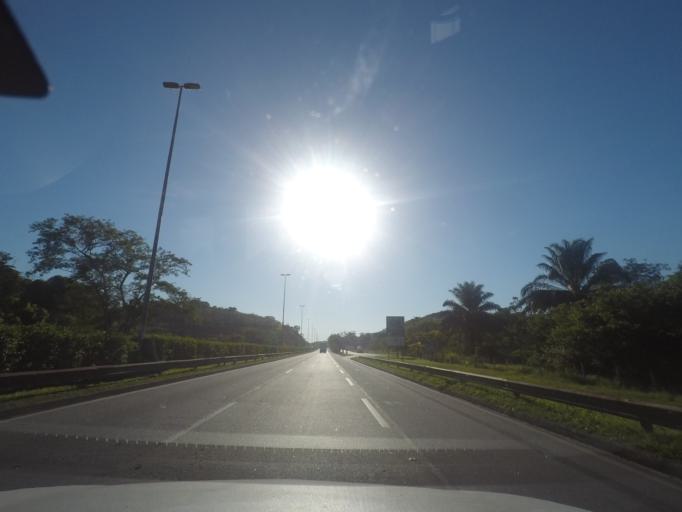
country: BR
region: Rio de Janeiro
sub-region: Petropolis
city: Petropolis
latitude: -22.6523
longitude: -43.1626
